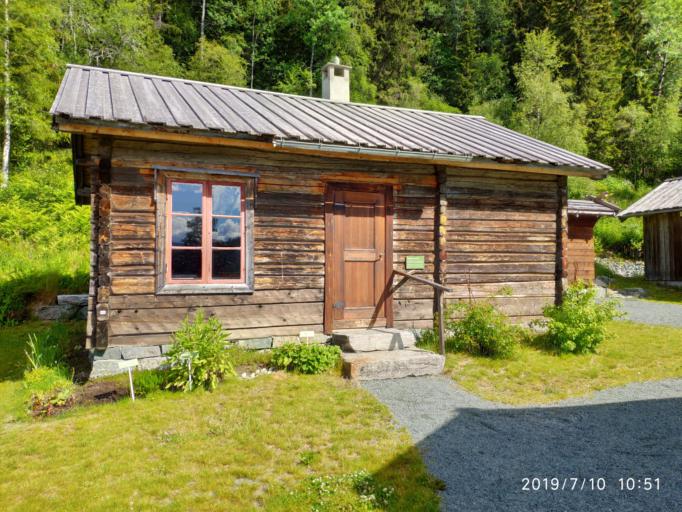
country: NO
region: Telemark
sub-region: Tokke
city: Dalen
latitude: 59.4667
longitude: 8.0199
